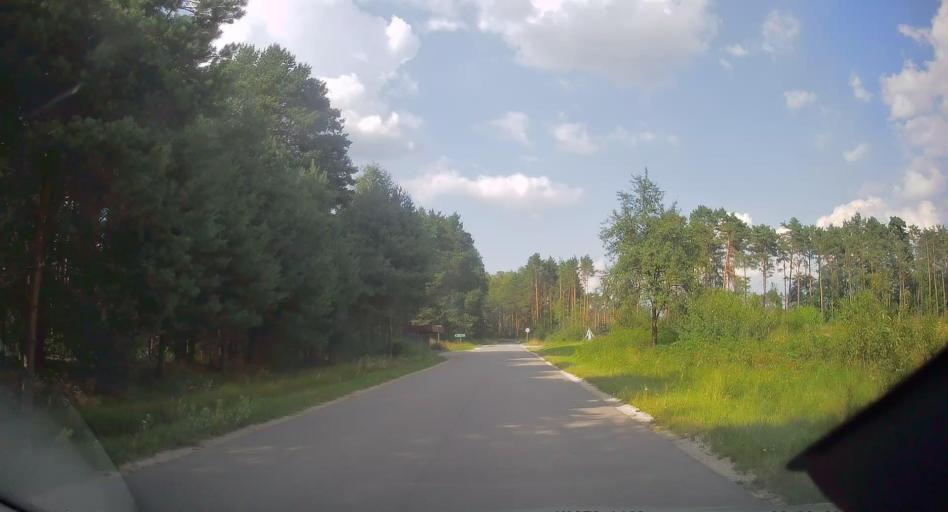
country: PL
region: Swietokrzyskie
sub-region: Powiat konecki
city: Radoszyce
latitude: 51.1014
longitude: 20.2650
